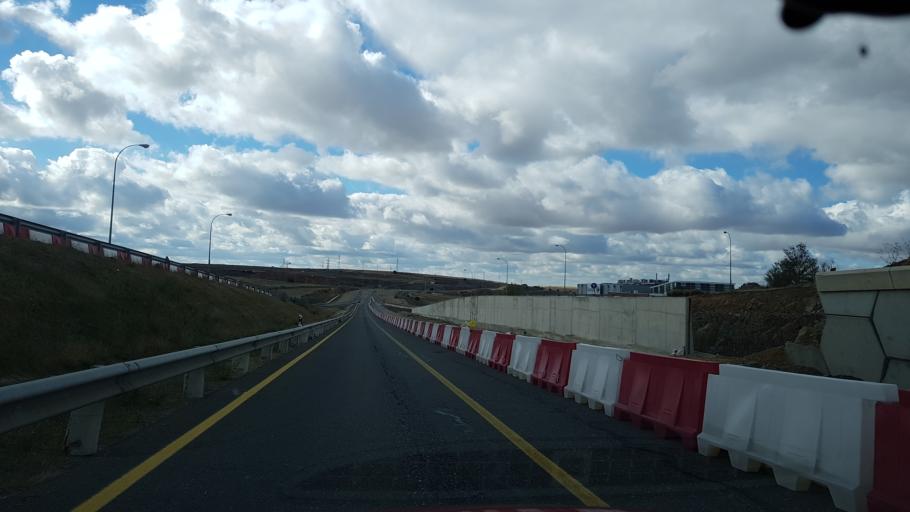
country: ES
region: Castille and Leon
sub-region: Provincia de Segovia
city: Segovia
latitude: 40.9200
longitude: -4.1085
